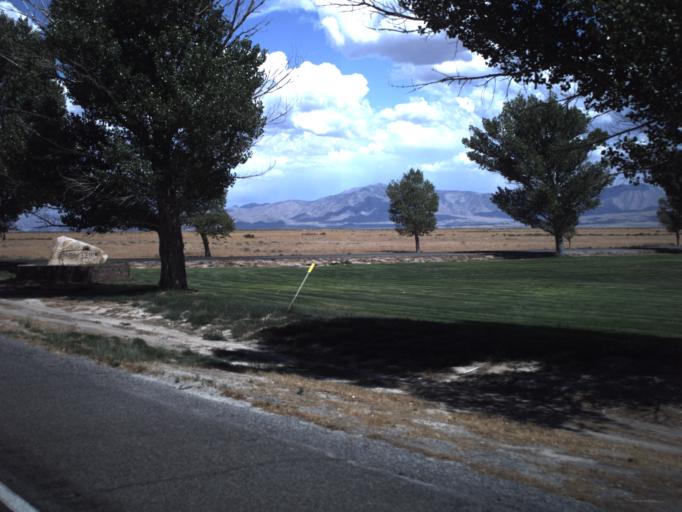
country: US
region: Utah
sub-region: Millard County
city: Delta
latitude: 39.3816
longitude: -112.5245
